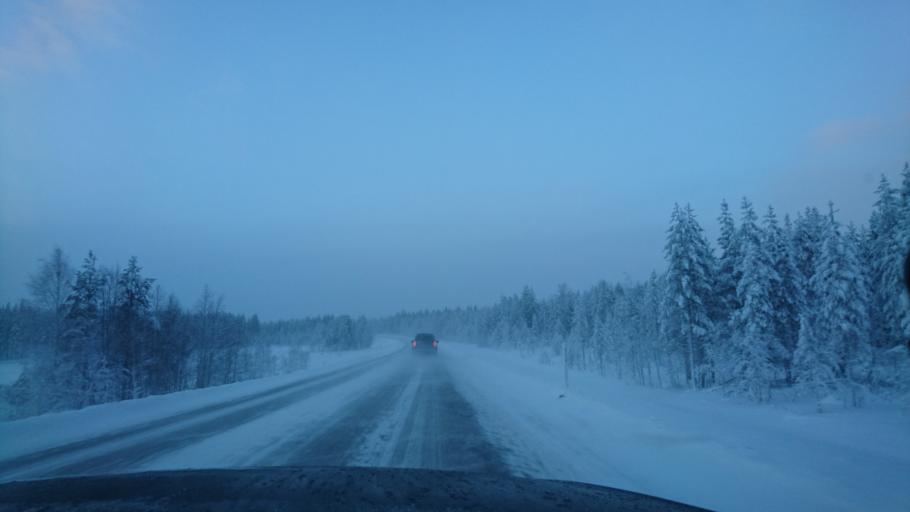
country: FI
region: Northern Ostrobothnia
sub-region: Koillismaa
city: Taivalkoski
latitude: 65.4763
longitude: 27.7657
